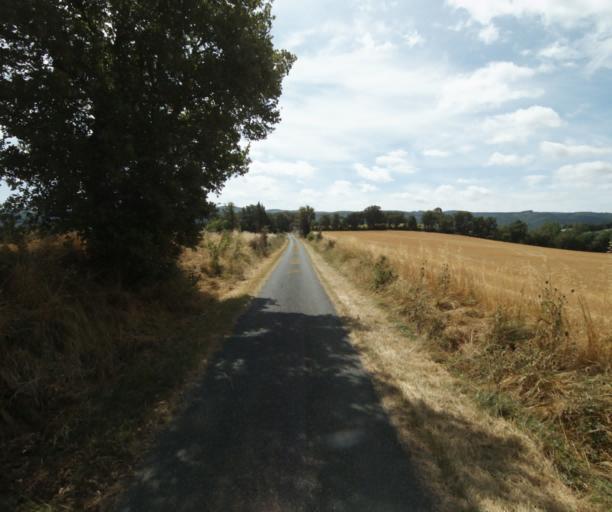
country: FR
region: Midi-Pyrenees
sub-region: Departement du Tarn
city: Dourgne
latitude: 43.4918
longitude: 2.1044
